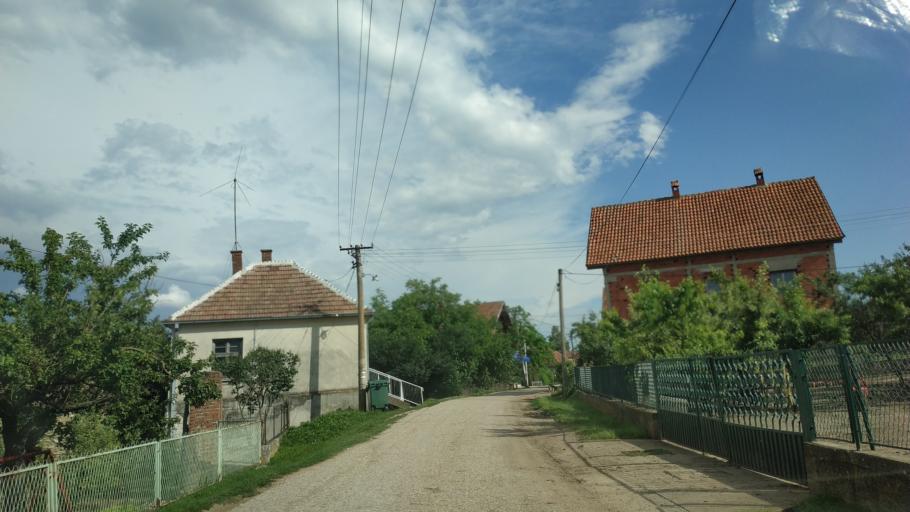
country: RS
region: Central Serbia
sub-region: Nisavski Okrug
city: Aleksinac
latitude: 43.6189
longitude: 21.6457
